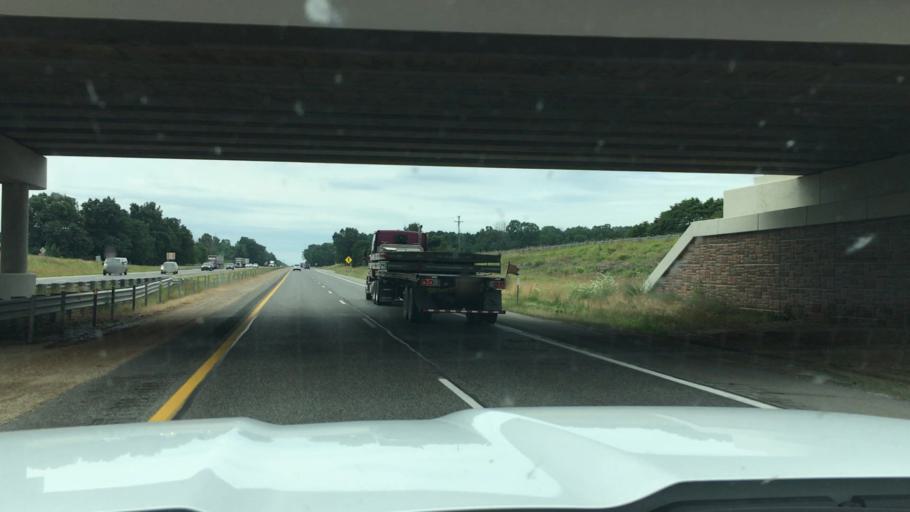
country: US
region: Michigan
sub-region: Allegan County
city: Otsego
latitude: 42.5372
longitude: -85.6602
